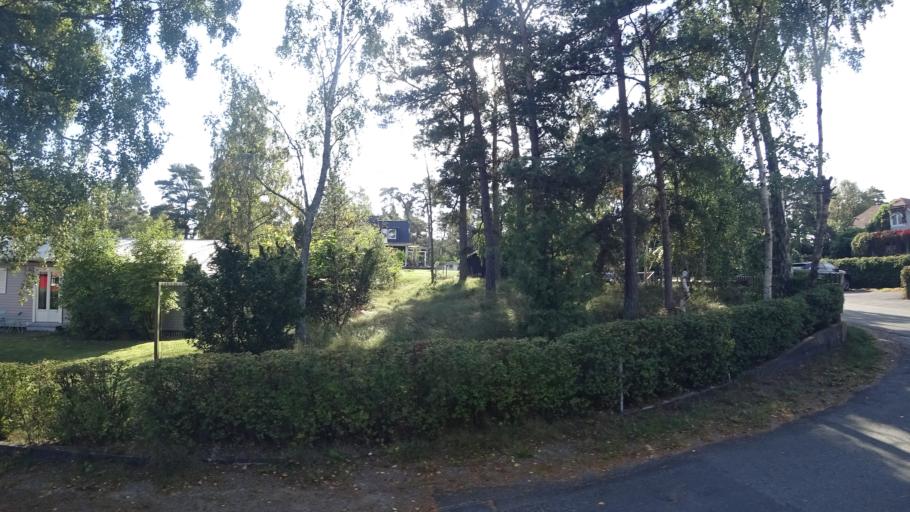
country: SE
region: Skane
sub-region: Kristianstads Kommun
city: Ahus
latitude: 55.9186
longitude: 14.3015
